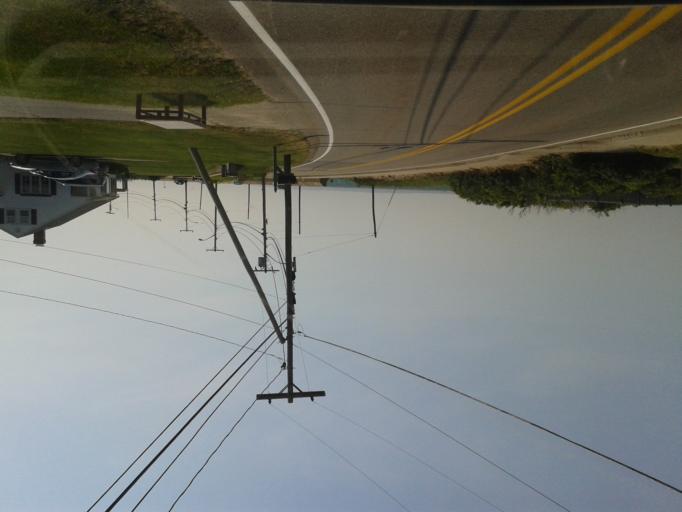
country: US
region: Massachusetts
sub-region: Barnstable County
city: Teaticket
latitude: 41.5466
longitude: -70.5773
